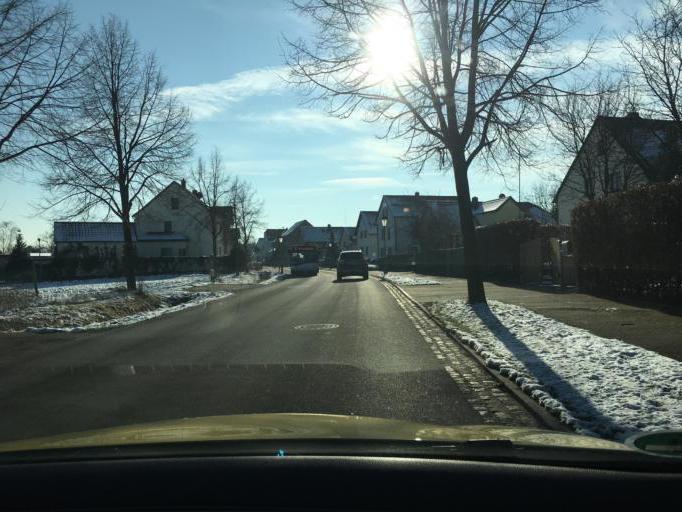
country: DE
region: Saxony
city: Grossposna
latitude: 51.2853
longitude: 12.5282
